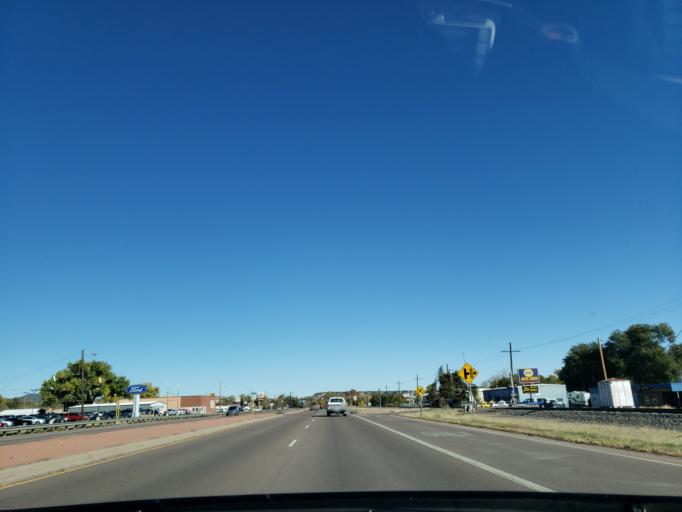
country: US
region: Colorado
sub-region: Fremont County
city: Lincoln Park
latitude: 38.4479
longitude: -105.2117
